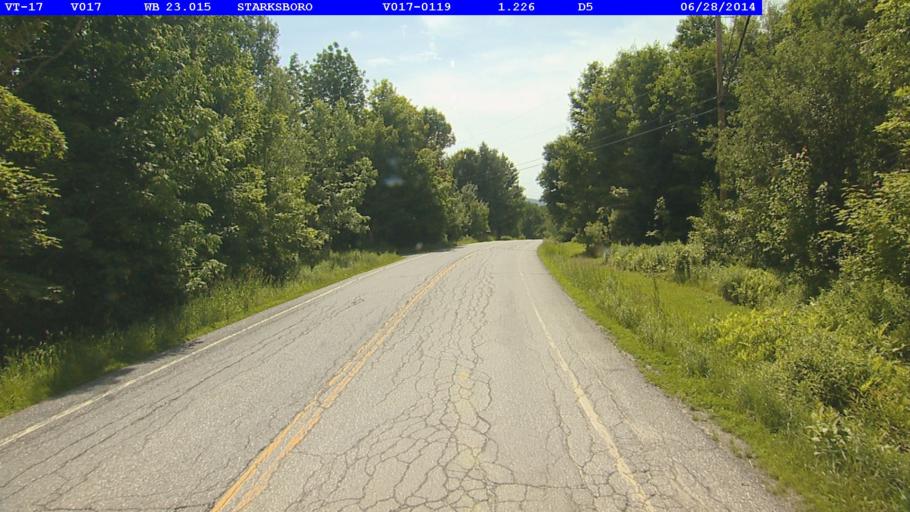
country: US
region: Vermont
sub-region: Addison County
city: Bristol
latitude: 44.1694
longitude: -72.9968
